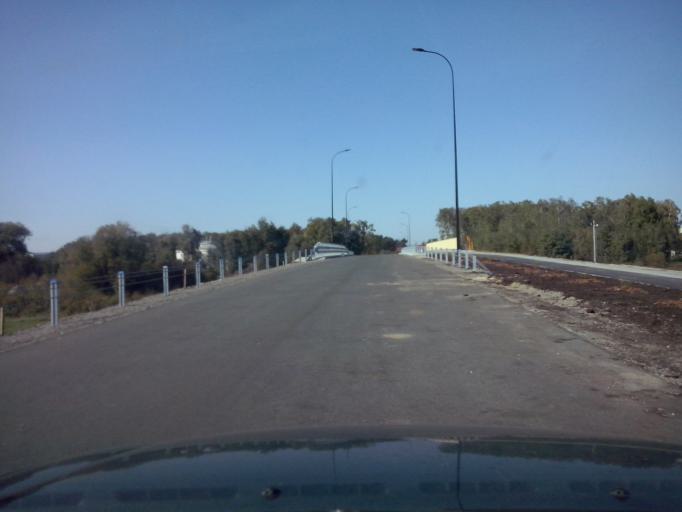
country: PL
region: Lublin Voivodeship
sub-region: Powiat bilgorajski
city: Bilgoraj
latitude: 50.5202
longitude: 22.7123
